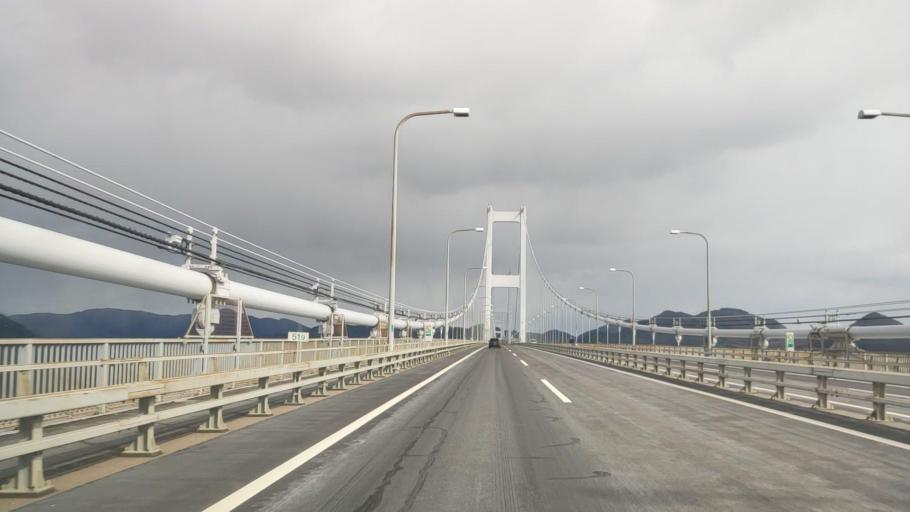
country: JP
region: Hiroshima
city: Takehara
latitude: 34.1151
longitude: 132.9838
